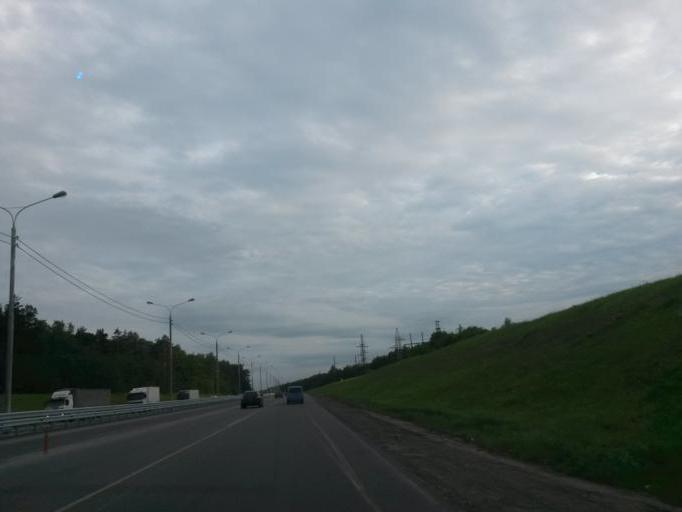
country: RU
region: Moskovskaya
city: L'vovskiy
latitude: 55.3087
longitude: 37.5511
